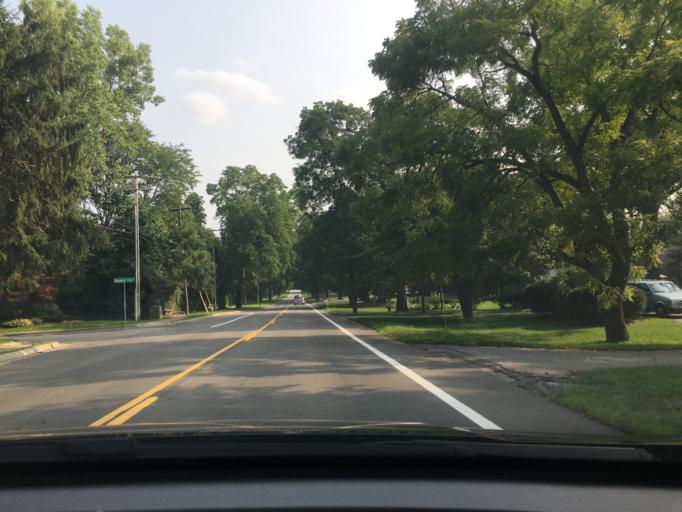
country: US
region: Michigan
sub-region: Oakland County
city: Bloomfield Hills
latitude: 42.5531
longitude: -83.2641
